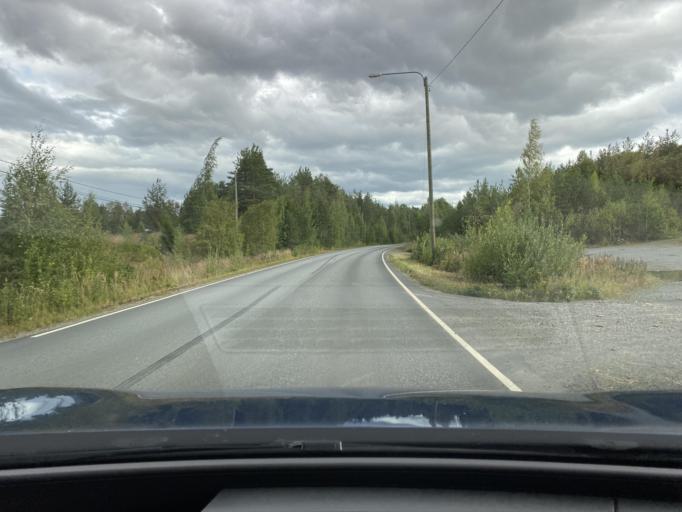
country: FI
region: Pirkanmaa
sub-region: Lounais-Pirkanmaa
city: Vammala
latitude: 61.3050
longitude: 22.9332
